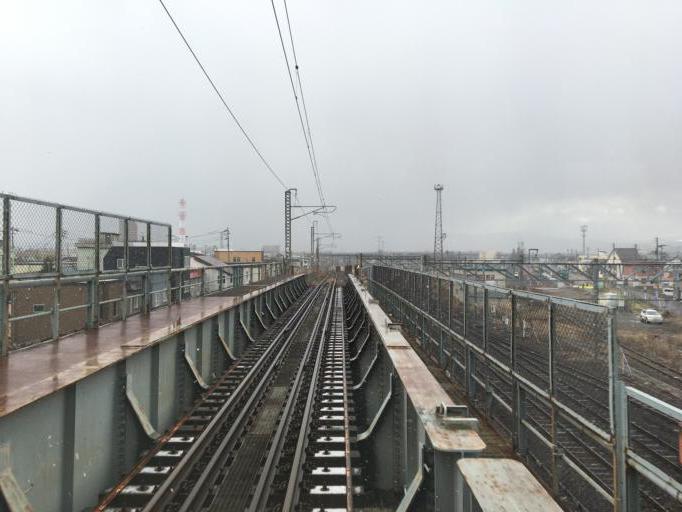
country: JP
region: Aomori
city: Aomori Shi
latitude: 40.8202
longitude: 140.7351
